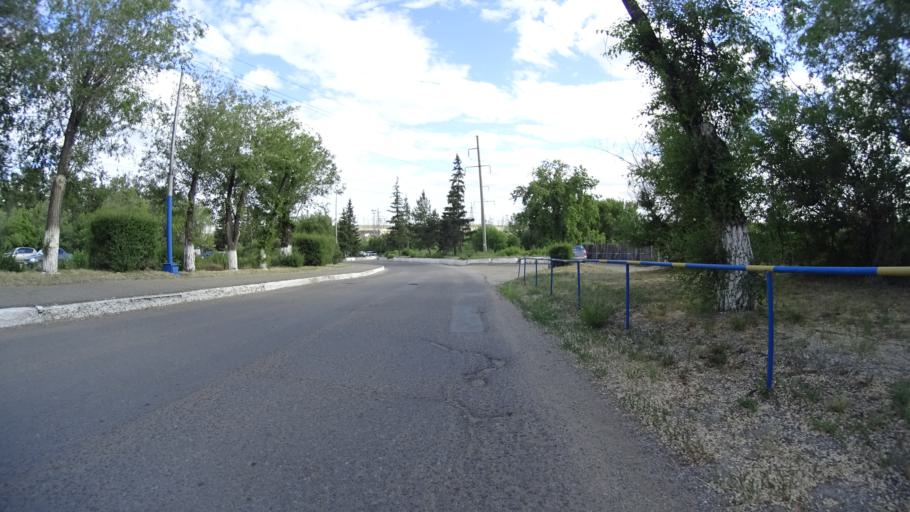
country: RU
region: Chelyabinsk
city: Troitsk
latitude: 54.0381
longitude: 61.6400
